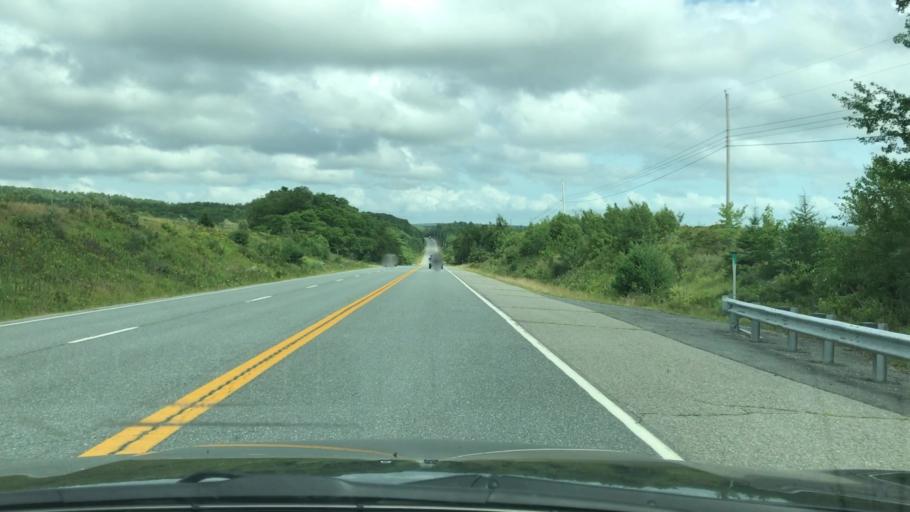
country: US
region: Maine
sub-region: Hancock County
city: Orland
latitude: 44.5670
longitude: -68.6179
